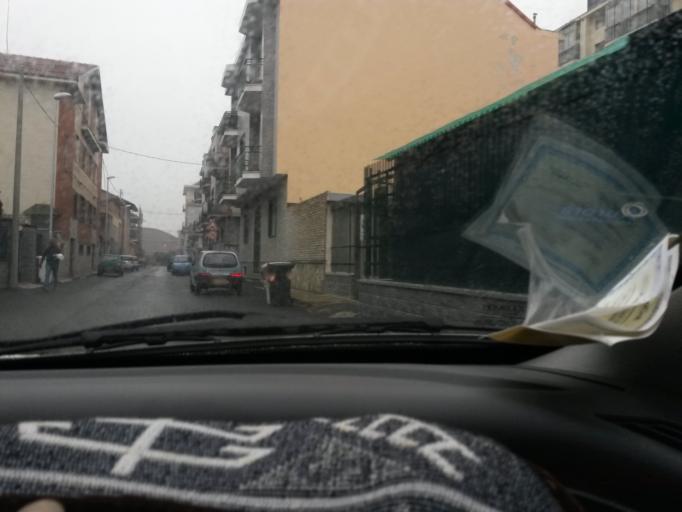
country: IT
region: Piedmont
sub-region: Provincia di Torino
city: Grugliasco
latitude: 45.0709
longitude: 7.5896
